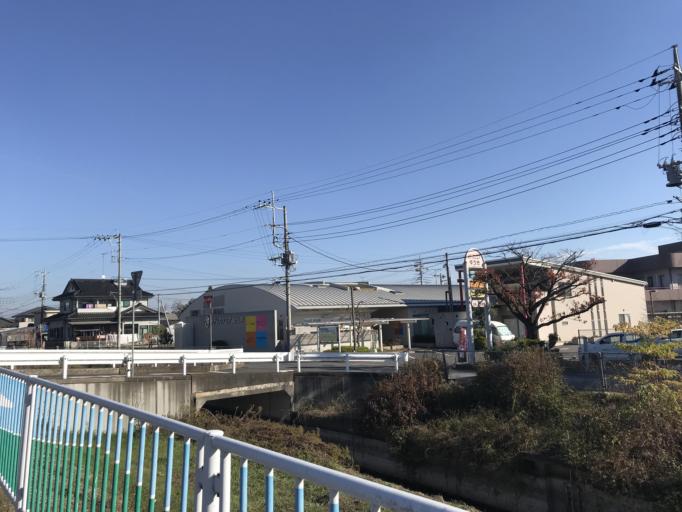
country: JP
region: Ibaraki
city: Yuki
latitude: 36.2863
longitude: 139.8591
